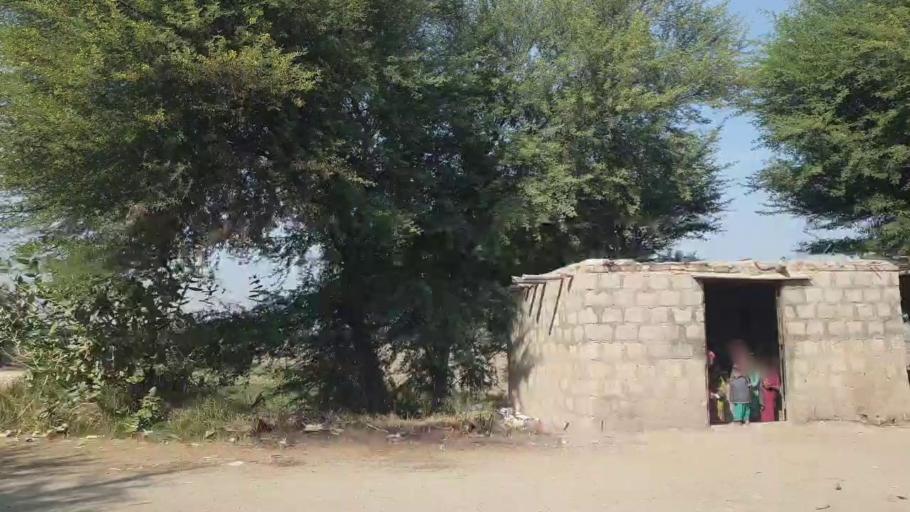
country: PK
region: Sindh
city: Matiari
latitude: 25.6759
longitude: 68.3575
